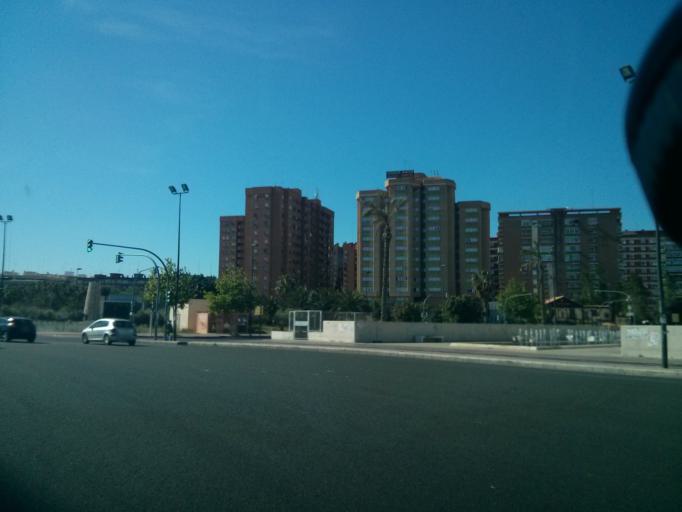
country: ES
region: Valencia
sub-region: Provincia de Valencia
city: Alboraya
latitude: 39.4815
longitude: -0.3520
